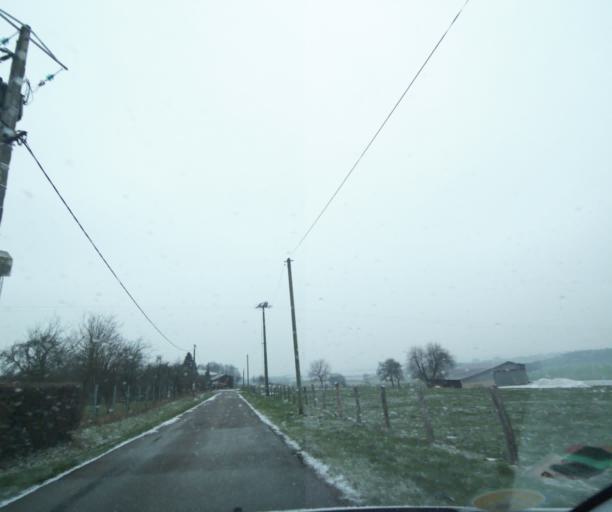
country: FR
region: Champagne-Ardenne
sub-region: Departement de la Haute-Marne
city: Wassy
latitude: 48.4618
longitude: 5.0321
